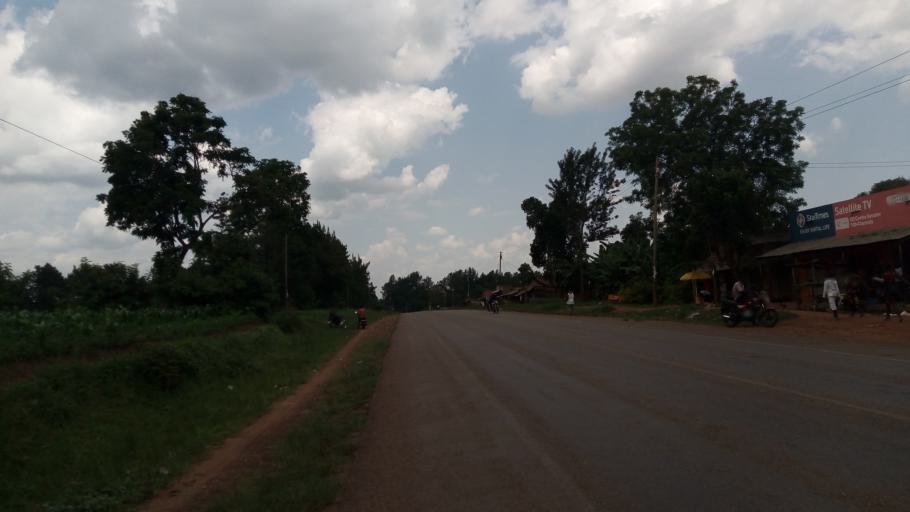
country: UG
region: Eastern Region
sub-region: Mbale District
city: Mbale
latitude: 1.0316
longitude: 34.1769
